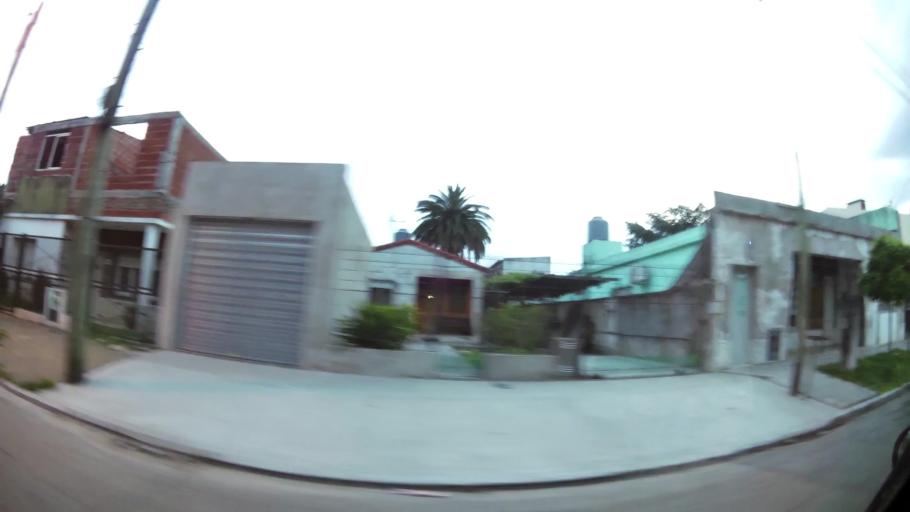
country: AR
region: Buenos Aires
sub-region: Partido de Quilmes
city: Quilmes
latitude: -34.7384
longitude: -58.2310
